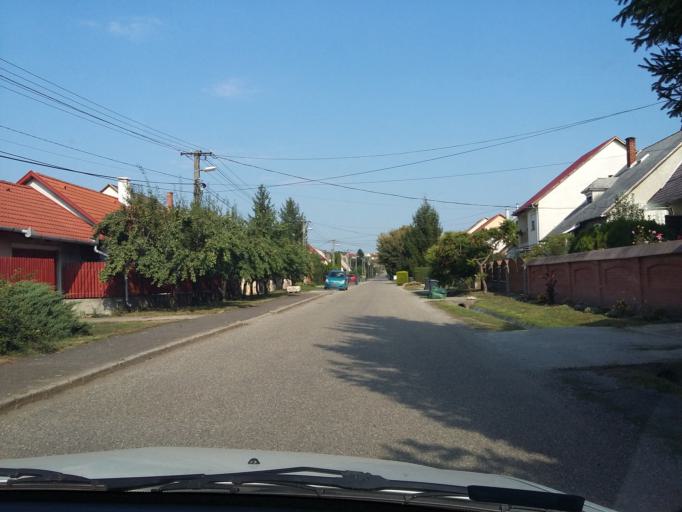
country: HU
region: Borsod-Abauj-Zemplen
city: Bekecs
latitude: 48.1501
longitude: 21.1827
